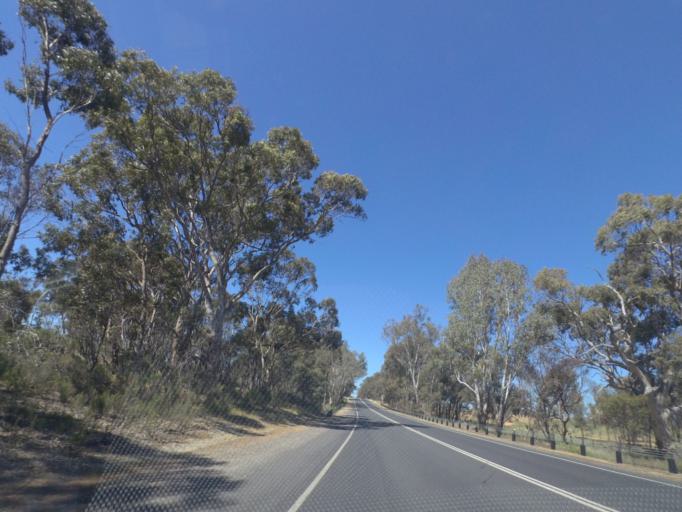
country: AU
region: Victoria
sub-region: Murrindindi
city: Kinglake West
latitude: -37.0293
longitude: 145.0730
